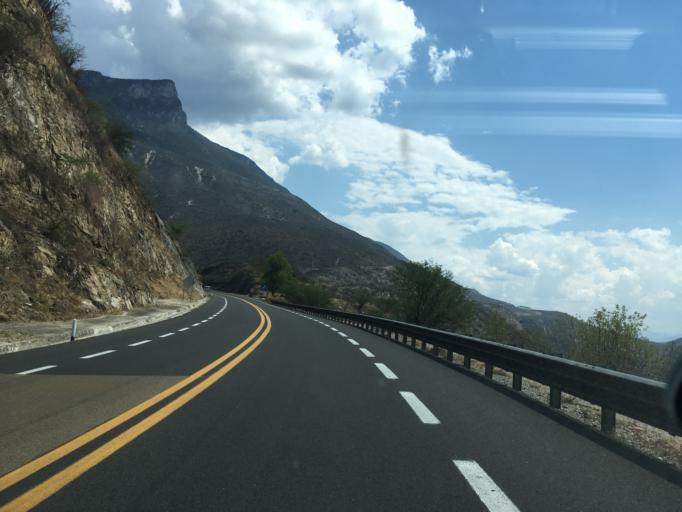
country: MX
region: Puebla
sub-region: San Jose Miahuatlan
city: San Pedro Tetitlan
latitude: 18.1532
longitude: -97.3054
